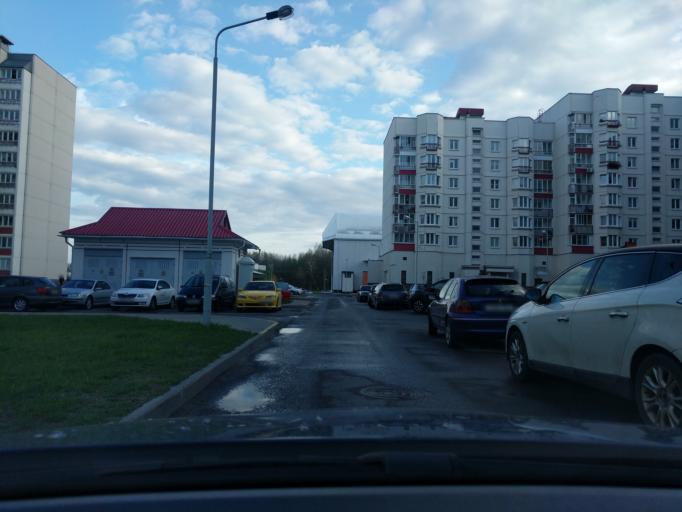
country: BY
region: Minsk
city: Novoye Medvezhino
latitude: 53.8947
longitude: 27.4608
